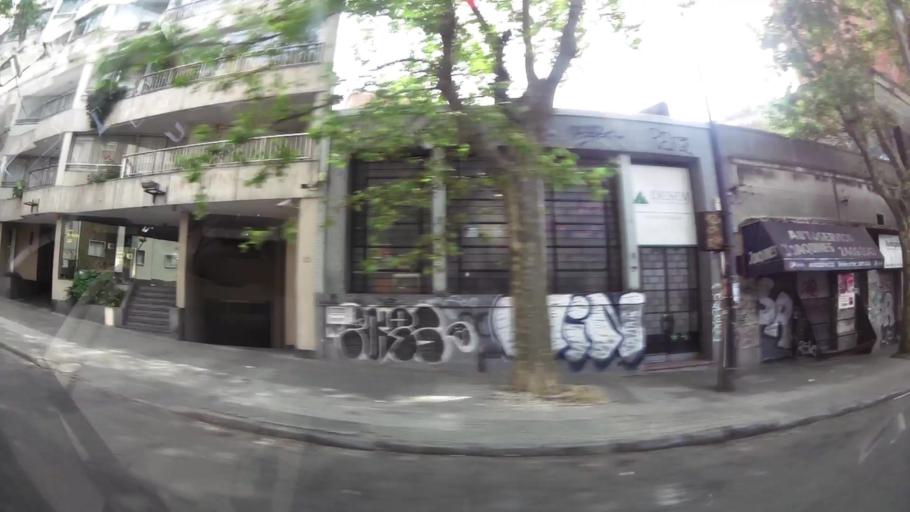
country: UY
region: Montevideo
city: Montevideo
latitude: -34.9091
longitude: -56.1687
